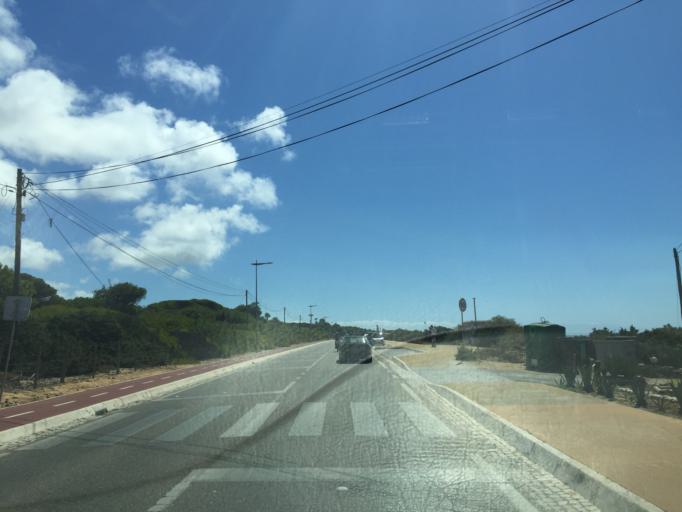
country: PT
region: Lisbon
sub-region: Cascais
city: Cascais
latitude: 38.7012
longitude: -9.4717
